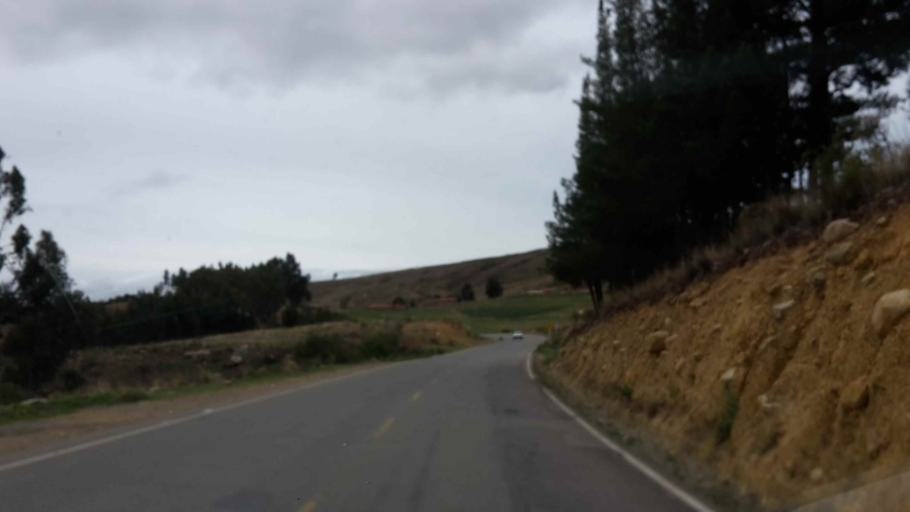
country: BO
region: Cochabamba
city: Arani
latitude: -17.4612
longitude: -65.6754
